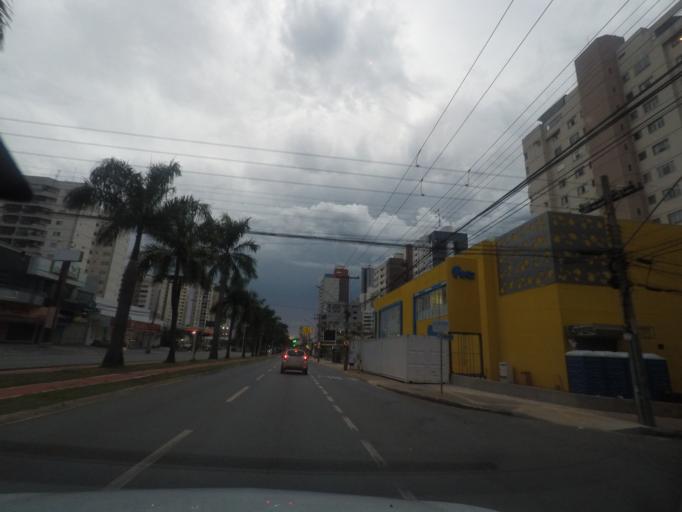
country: BR
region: Goias
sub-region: Goiania
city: Goiania
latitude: -16.7141
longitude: -49.2681
